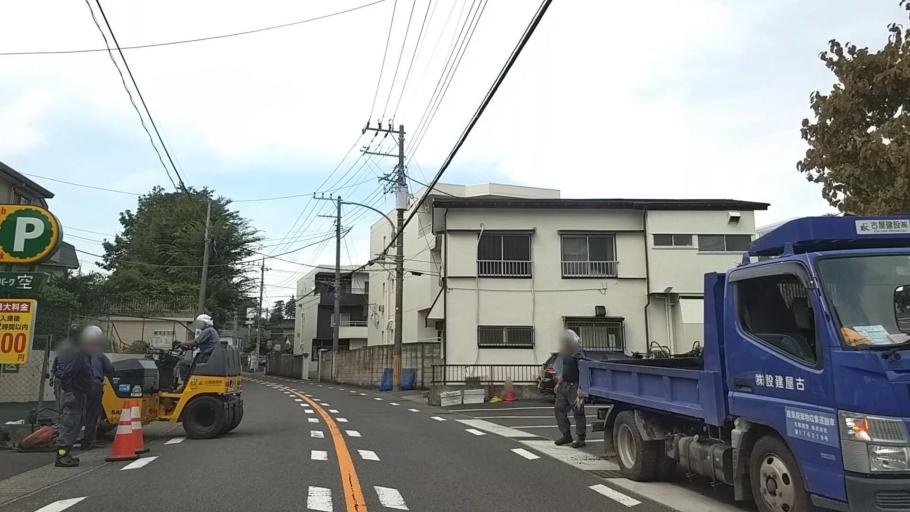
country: JP
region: Kanagawa
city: Yokohama
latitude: 35.4825
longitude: 139.5709
